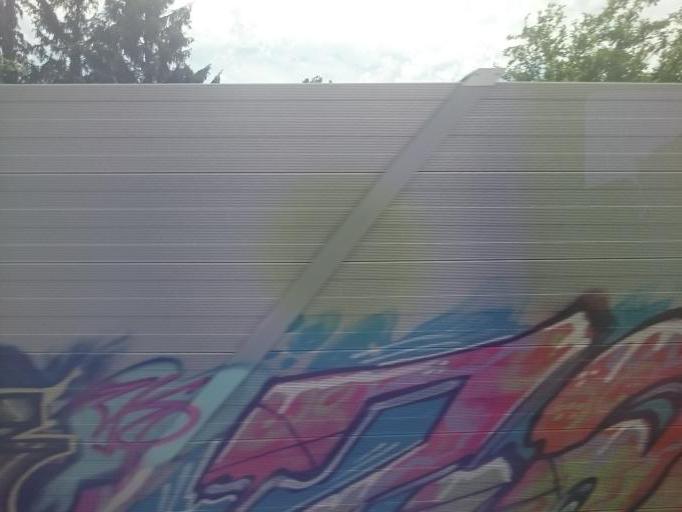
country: DE
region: Bavaria
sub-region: Upper Bavaria
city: Bogenhausen
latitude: 48.1327
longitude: 11.6438
